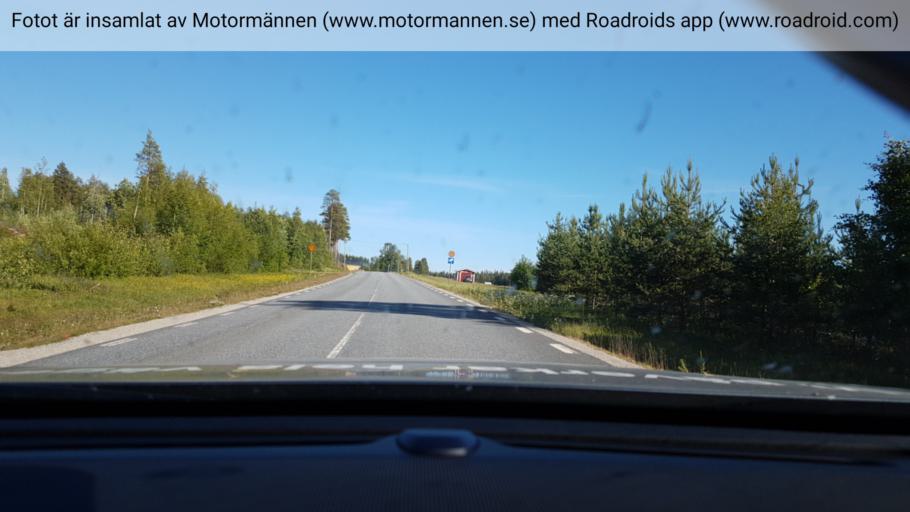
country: SE
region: Vaesterbotten
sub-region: Lycksele Kommun
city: Lycksele
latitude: 64.3998
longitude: 19.0377
